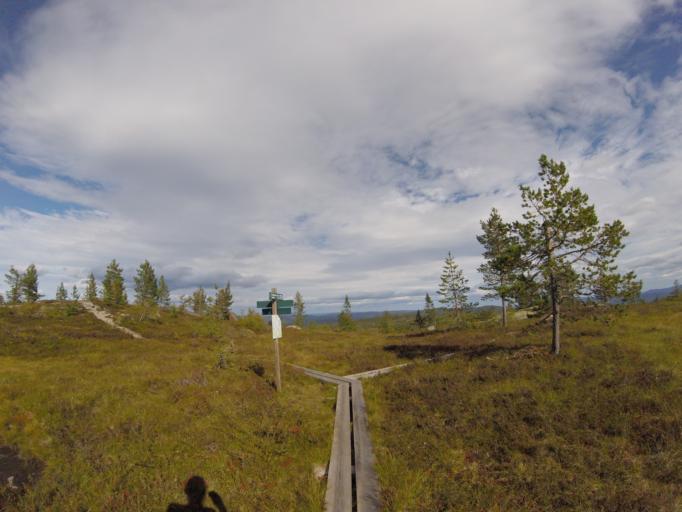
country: NO
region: Buskerud
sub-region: Flesberg
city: Lampeland
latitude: 59.7601
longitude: 9.4293
